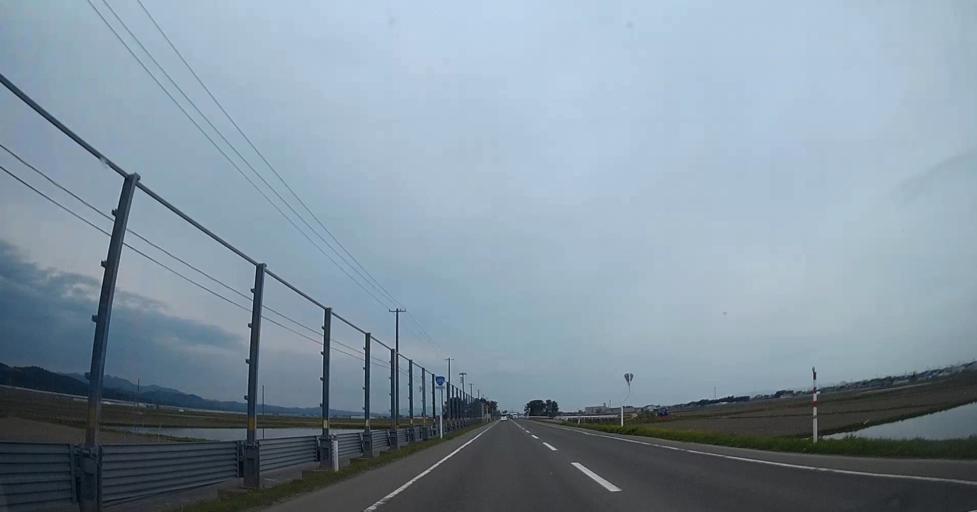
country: JP
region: Aomori
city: Aomori Shi
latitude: 40.8925
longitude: 140.6685
